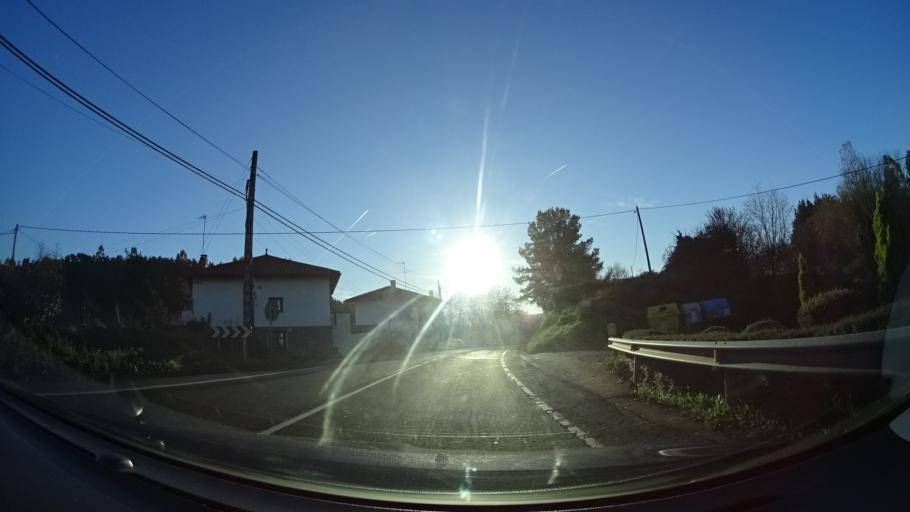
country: ES
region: Basque Country
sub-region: Bizkaia
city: Kortezubi
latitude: 43.3298
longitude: -2.6599
